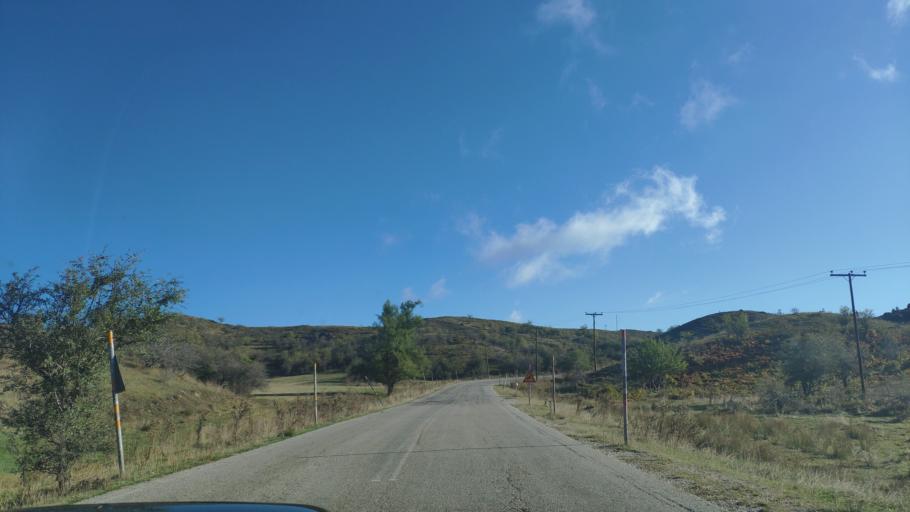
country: GR
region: Epirus
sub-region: Nomos Ioanninon
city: Metsovo
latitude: 39.7888
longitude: 21.1600
